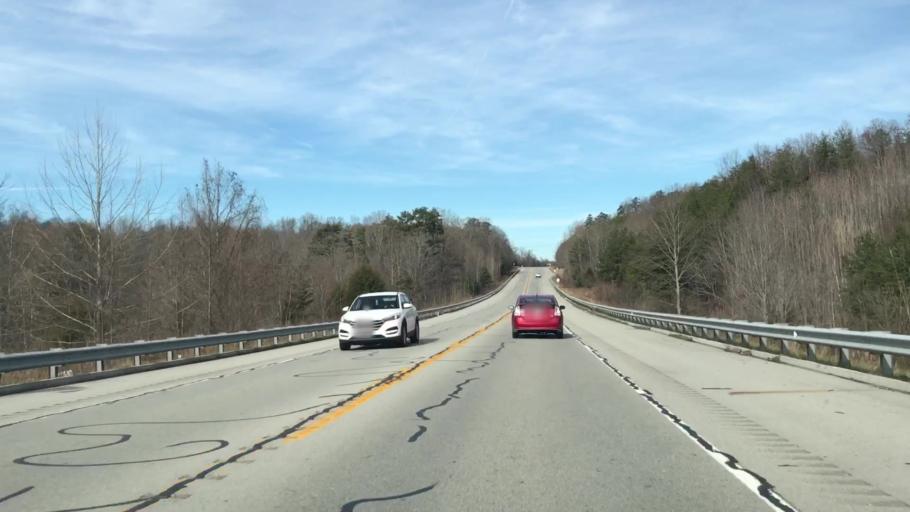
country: US
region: Kentucky
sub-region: McCreary County
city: Whitley City
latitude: 36.8018
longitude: -84.4863
